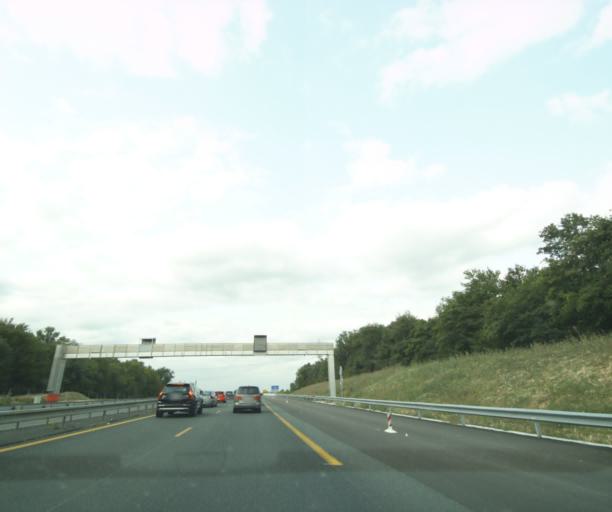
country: FR
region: Centre
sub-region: Departement d'Indre-et-Loire
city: Chambray-les-Tours
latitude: 47.3205
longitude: 0.6900
